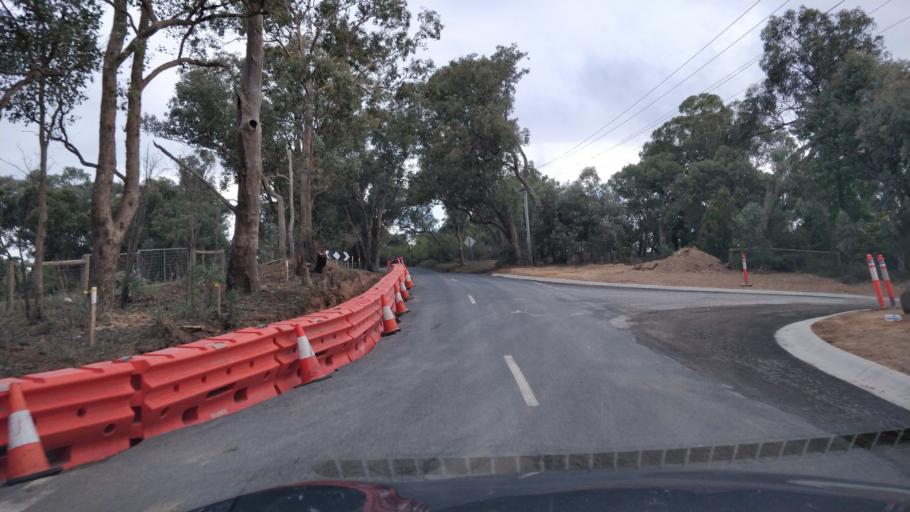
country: AU
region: Victoria
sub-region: Nillumbik
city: Research
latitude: -37.6912
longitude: 145.1791
